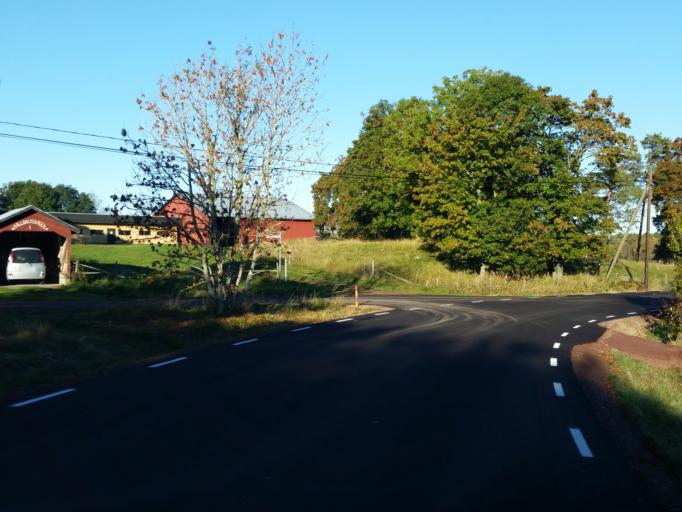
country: AX
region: Alands landsbygd
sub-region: Sund
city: Sund
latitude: 60.2227
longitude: 20.0924
